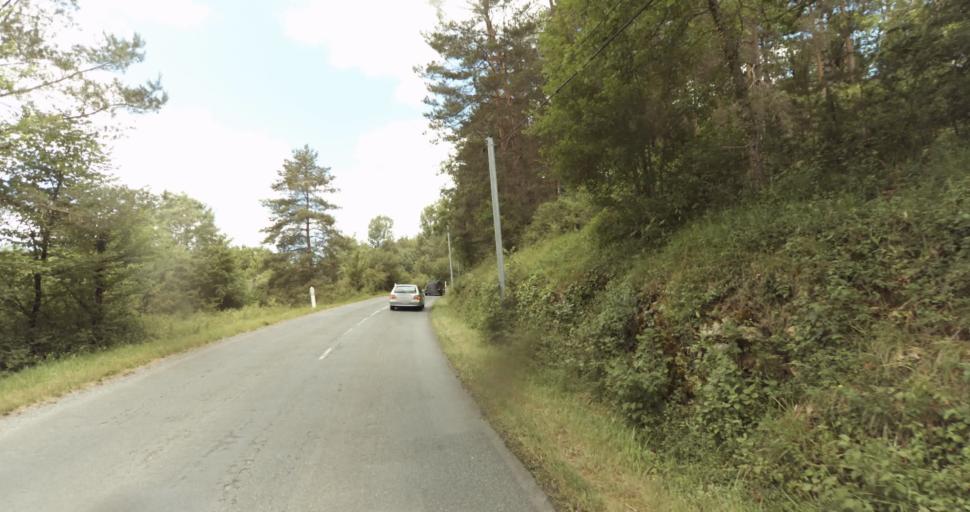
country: FR
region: Aquitaine
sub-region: Departement de la Dordogne
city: Beaumont-du-Perigord
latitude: 44.7624
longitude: 0.7629
